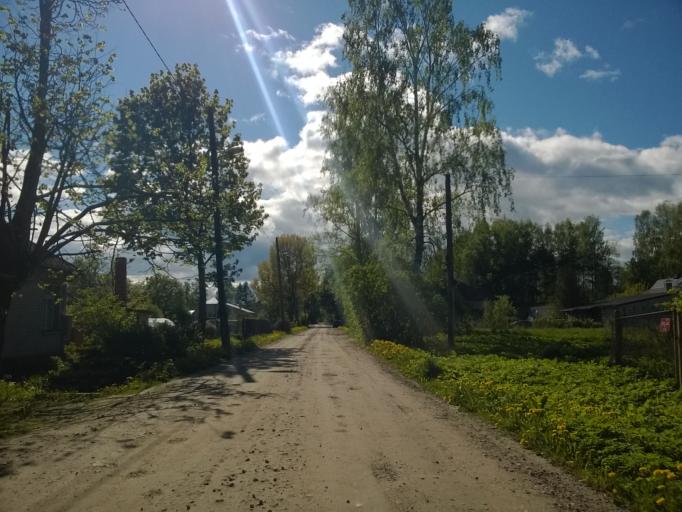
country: LV
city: Tireli
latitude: 56.9536
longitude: 23.6297
